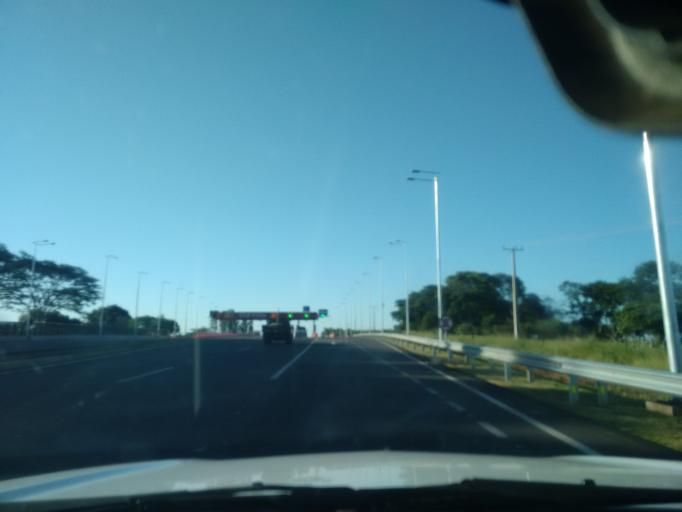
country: BR
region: Mato Grosso do Sul
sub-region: Eldorado
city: Eldorado
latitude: -23.8664
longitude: -54.3289
